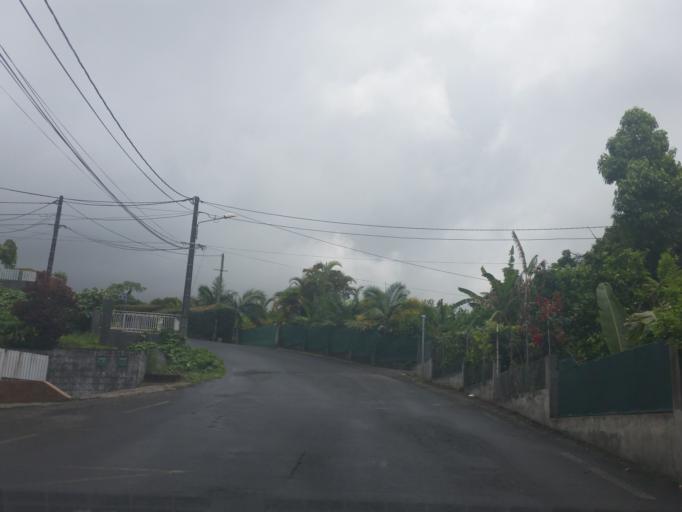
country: RE
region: Reunion
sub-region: Reunion
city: Le Tampon
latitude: -21.2426
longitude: 55.5135
